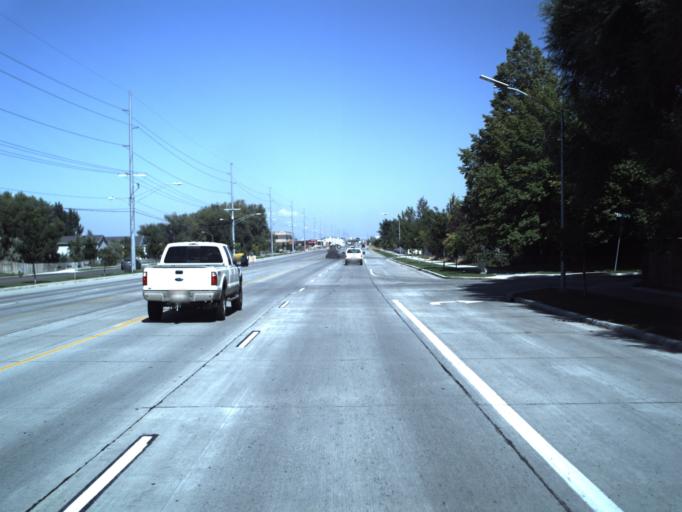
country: US
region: Utah
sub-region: Cache County
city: Logan
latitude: 41.7244
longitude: -111.8599
